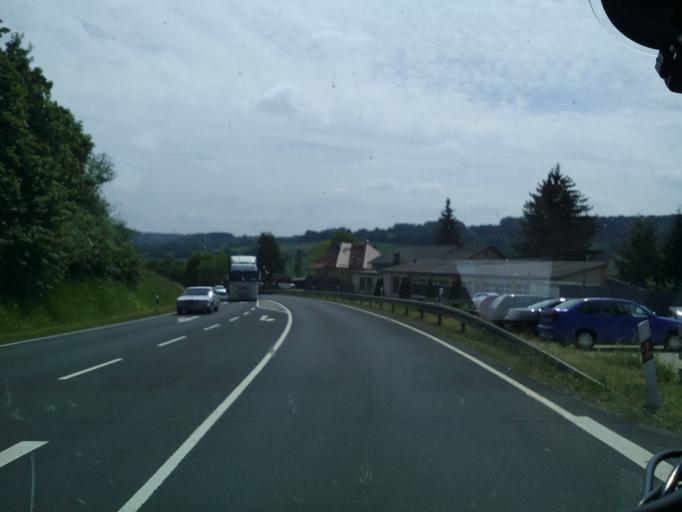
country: DE
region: Bavaria
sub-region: Upper Franconia
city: Weissenbrunn
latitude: 50.2062
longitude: 11.3216
